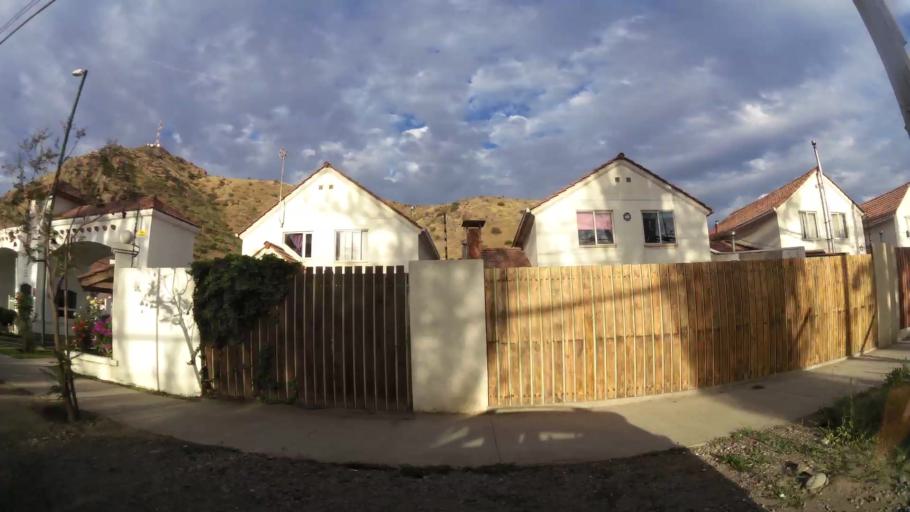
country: CL
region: Santiago Metropolitan
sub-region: Provincia de Maipo
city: San Bernardo
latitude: -33.6294
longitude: -70.6782
